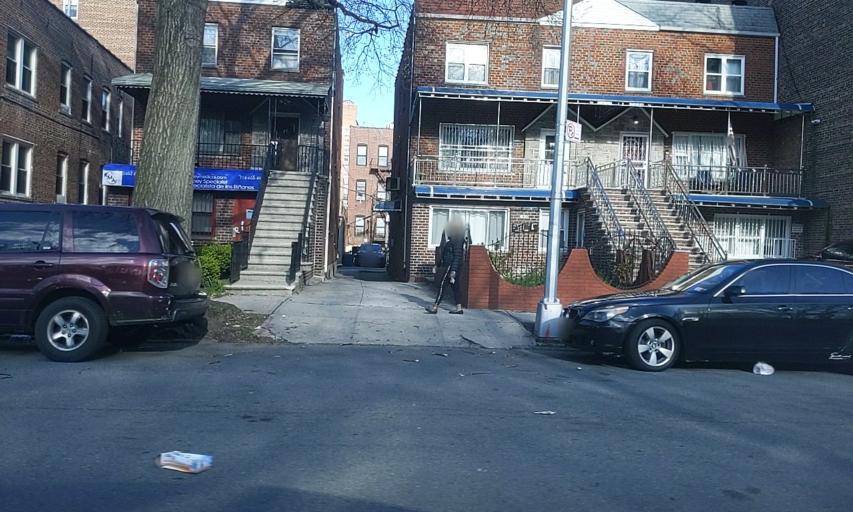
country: US
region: New York
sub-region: Bronx
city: The Bronx
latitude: 40.8629
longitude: -73.8705
